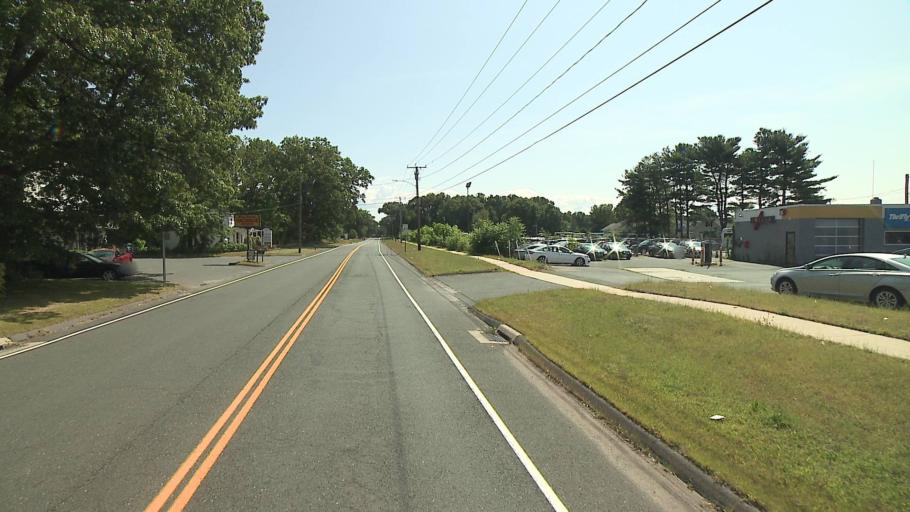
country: US
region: Connecticut
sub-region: Hartford County
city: Windsor Locks
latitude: 41.9294
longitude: -72.6691
